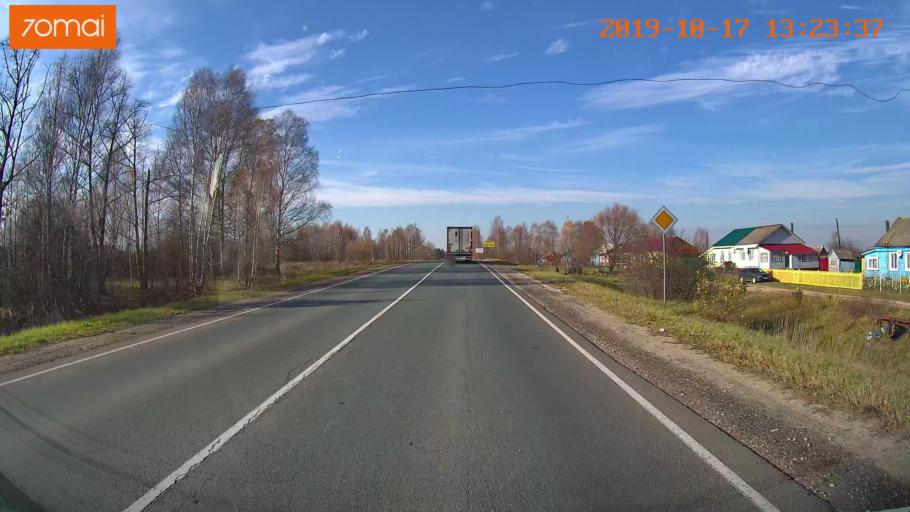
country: RU
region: Rjazan
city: Gus'-Zheleznyy
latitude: 55.0904
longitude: 40.9768
